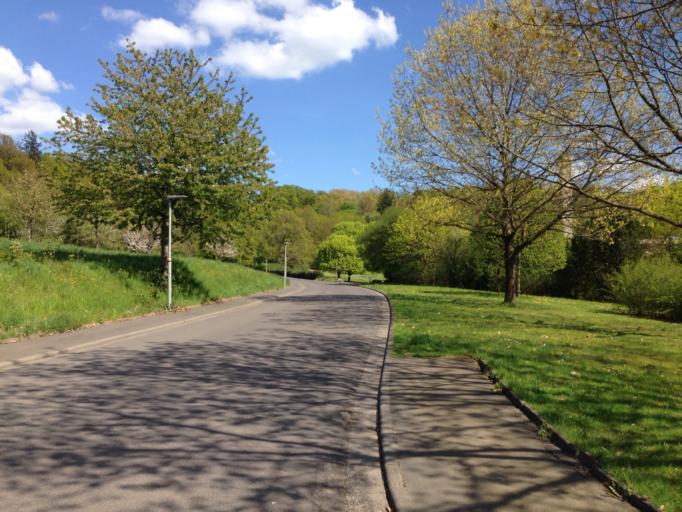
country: DE
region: Hesse
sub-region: Regierungsbezirk Giessen
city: Laubach
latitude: 50.5506
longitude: 8.9878
